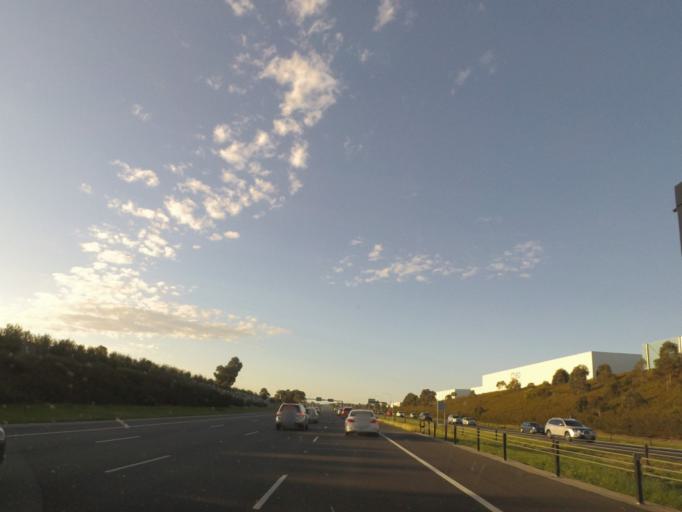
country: AU
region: Victoria
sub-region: Monash
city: Mulgrave
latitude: -37.9111
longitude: 145.2160
